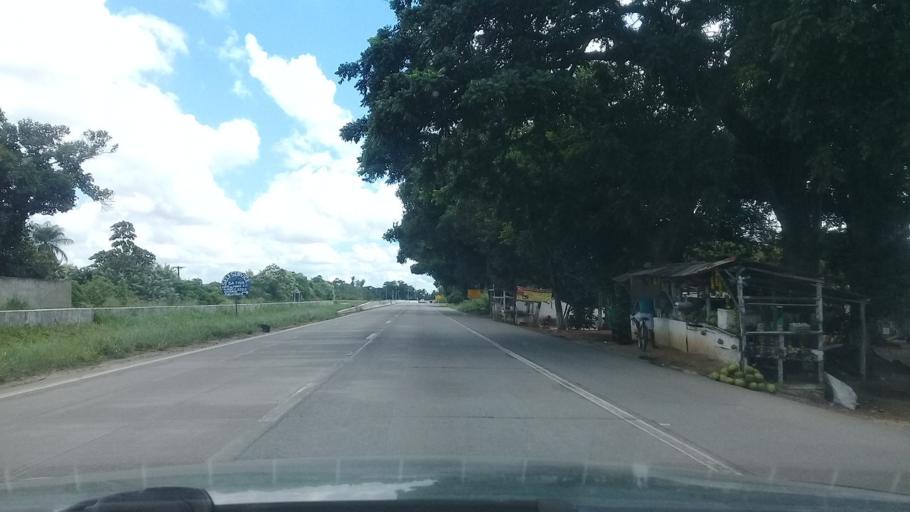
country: BR
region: Pernambuco
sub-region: Sao Lourenco Da Mata
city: Sao Lourenco da Mata
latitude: -7.9379
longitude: -35.1271
